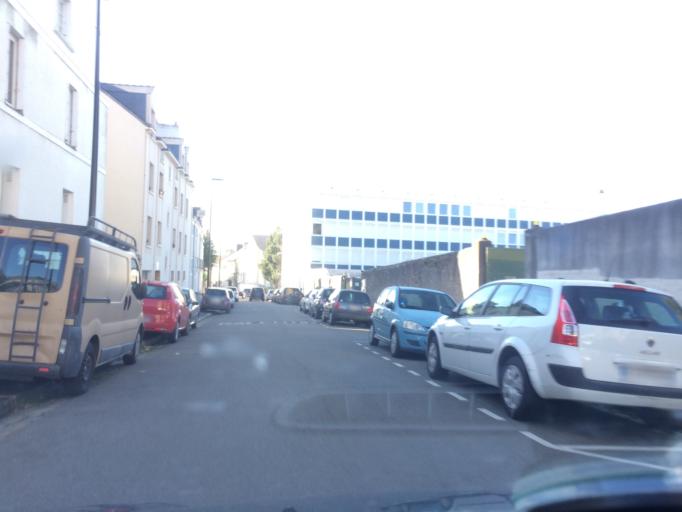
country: FR
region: Pays de la Loire
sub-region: Departement de la Loire-Atlantique
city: Nantes
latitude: 47.2292
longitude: -1.5430
